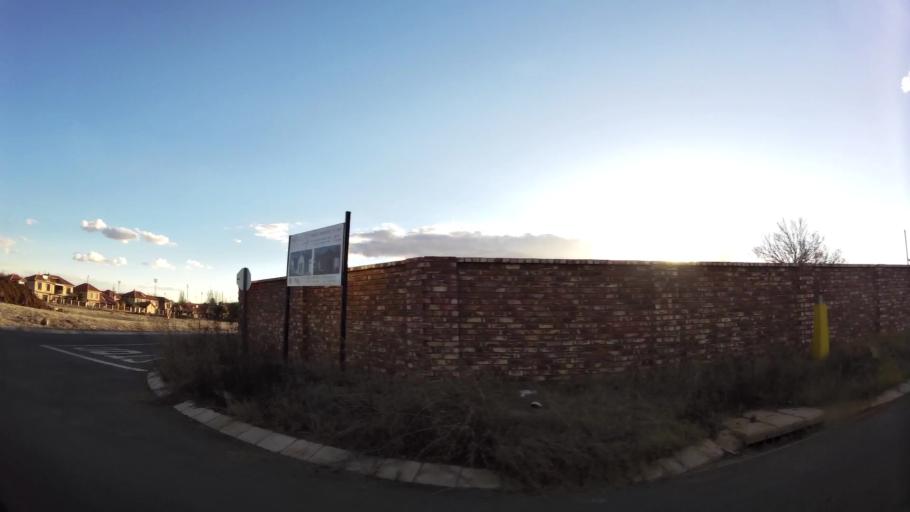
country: ZA
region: North-West
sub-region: Dr Kenneth Kaunda District Municipality
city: Potchefstroom
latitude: -26.6804
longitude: 27.1014
